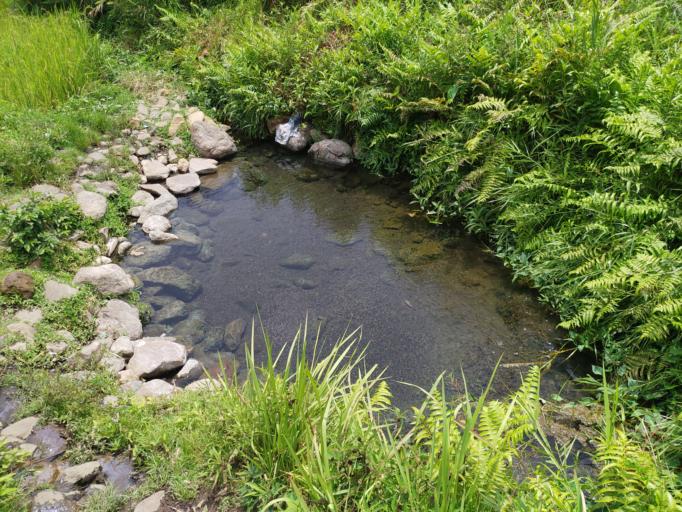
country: ID
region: East Nusa Tenggara
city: Koanara
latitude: -8.7439
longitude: 121.8355
